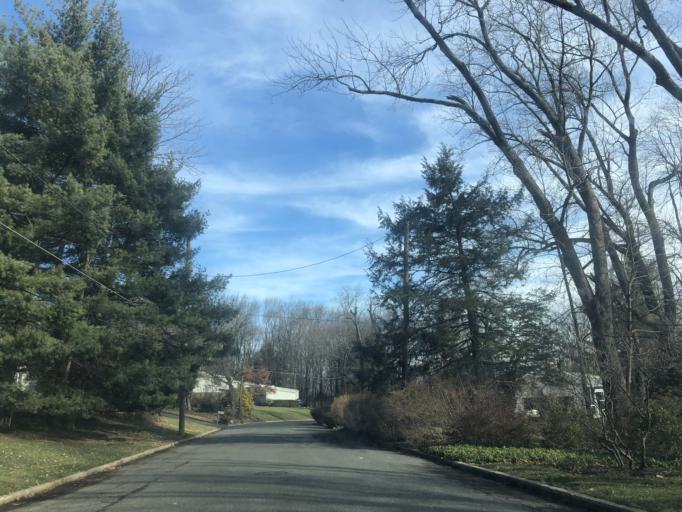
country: US
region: New Jersey
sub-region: Somerset County
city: Kingston
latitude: 40.3559
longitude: -74.6323
